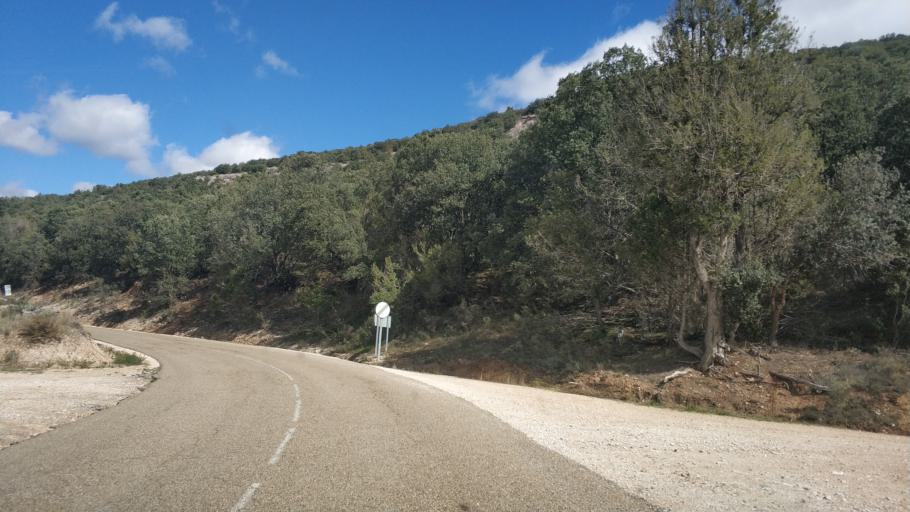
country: ES
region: Castille and Leon
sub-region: Provincia de Burgos
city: Retuerta
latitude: 42.0380
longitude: -3.4786
